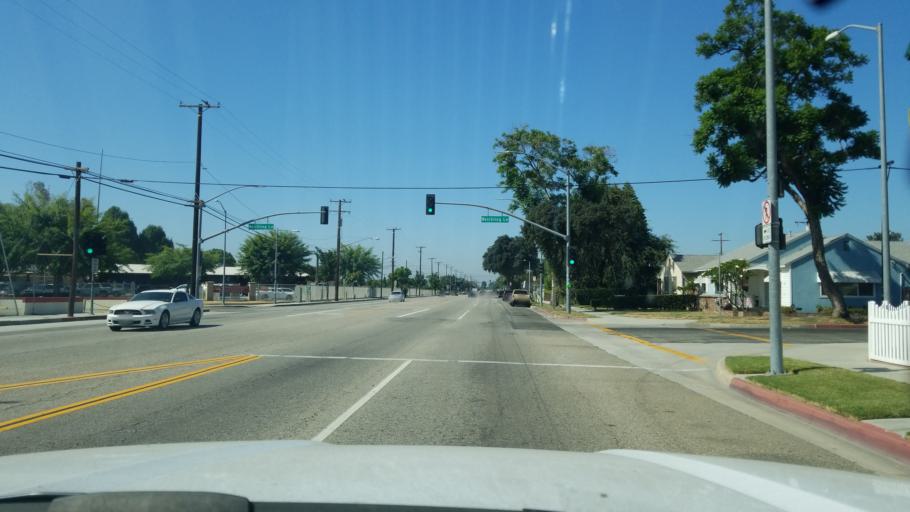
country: US
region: California
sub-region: Los Angeles County
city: West Whittier-Los Nietos
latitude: 33.9851
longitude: -118.0689
